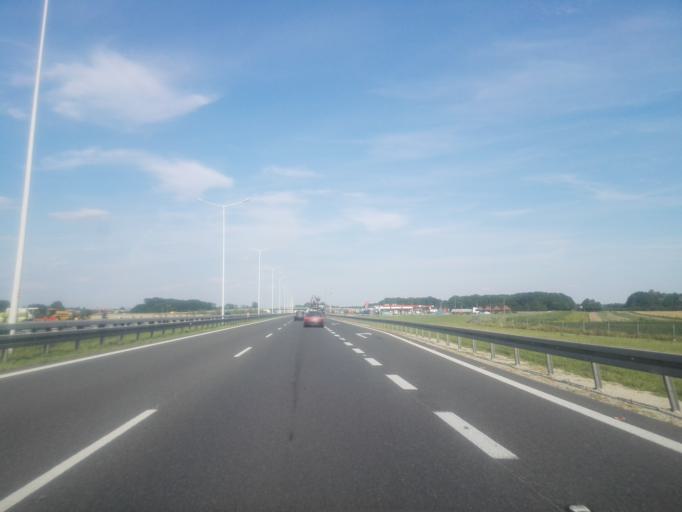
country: PL
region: Lower Silesian Voivodeship
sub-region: Powiat wroclawski
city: Dlugoleka
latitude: 51.2254
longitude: 17.1948
